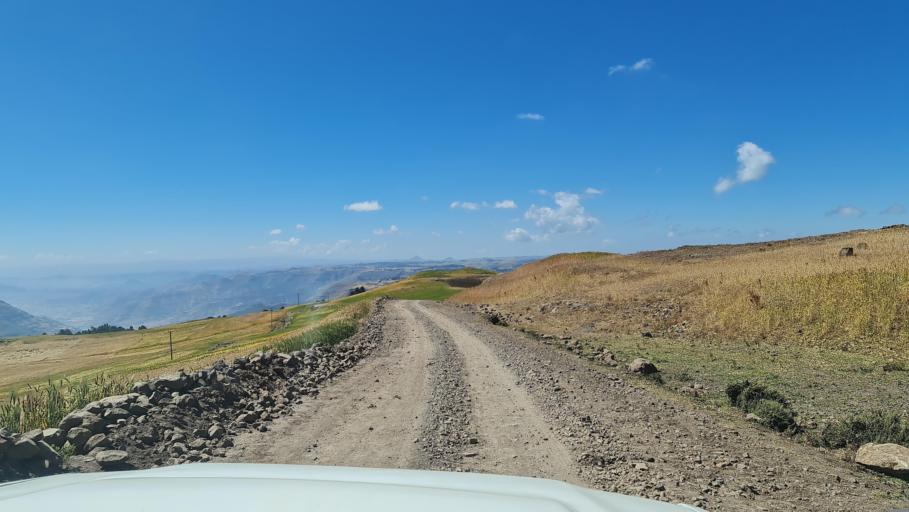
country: ET
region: Amhara
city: Debark'
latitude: 13.2336
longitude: 38.1046
